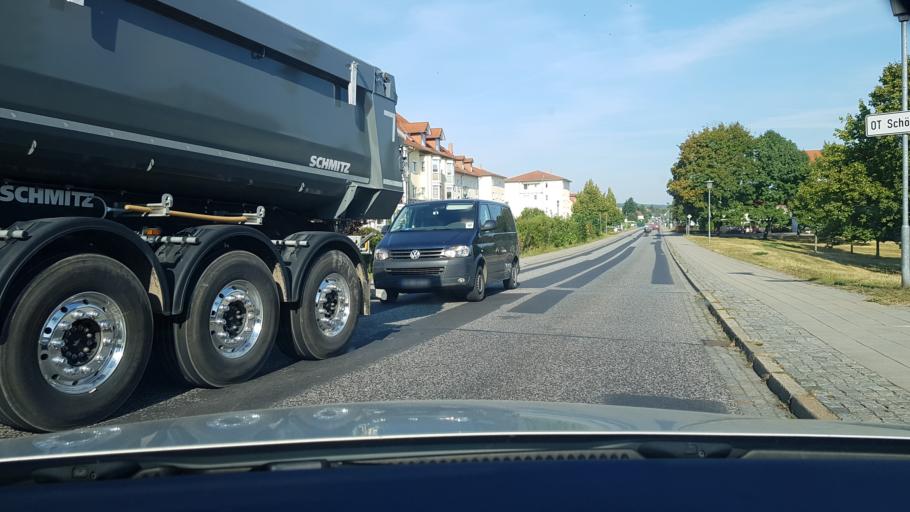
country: DE
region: Brandenburg
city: Eisenhuettenstadt
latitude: 52.1469
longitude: 14.6178
